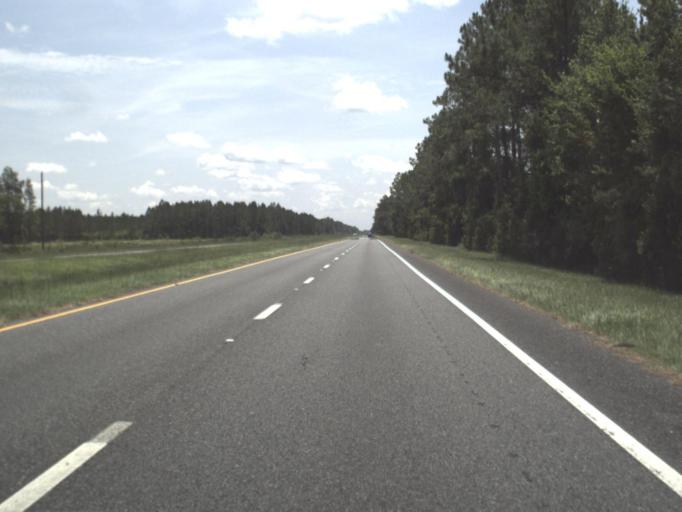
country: US
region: Florida
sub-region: Taylor County
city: Steinhatchee
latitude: 29.7145
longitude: -83.3007
